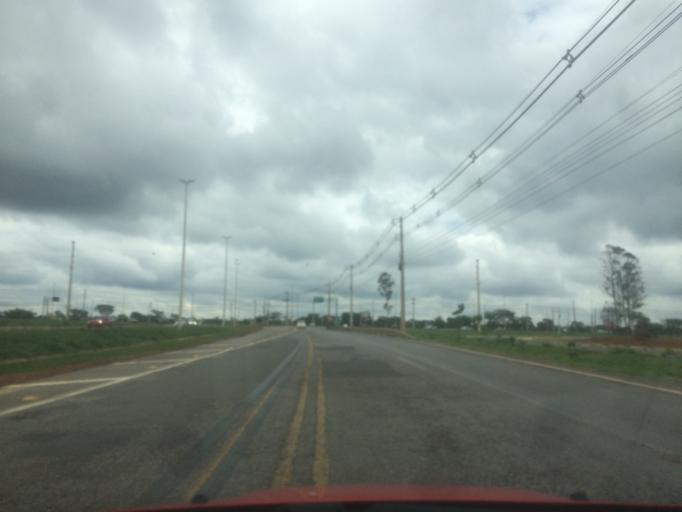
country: BR
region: Federal District
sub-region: Brasilia
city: Brasilia
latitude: -15.8850
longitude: -47.8195
